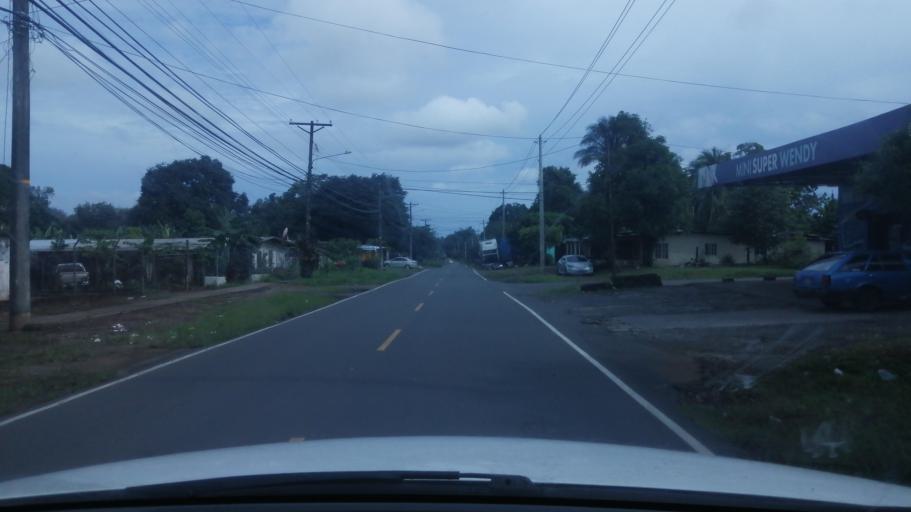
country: PA
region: Chiriqui
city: David
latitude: 8.4167
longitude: -82.4263
